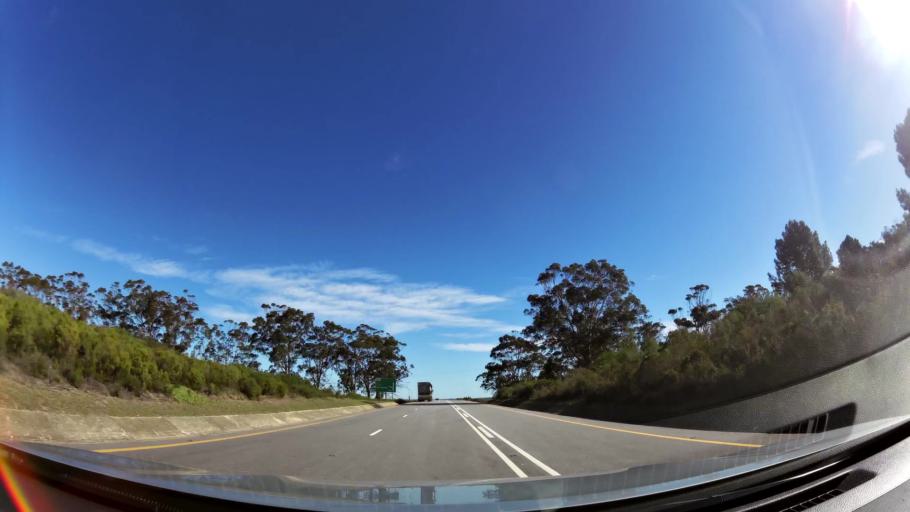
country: ZA
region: Eastern Cape
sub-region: Cacadu District Municipality
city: Kruisfontein
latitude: -34.0199
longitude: 24.6187
